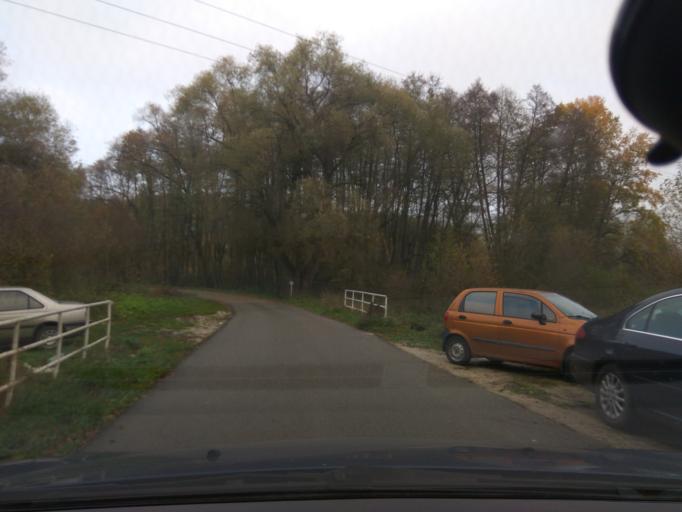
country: SK
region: Trnavsky
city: Vrbove
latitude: 48.6931
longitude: 17.6924
